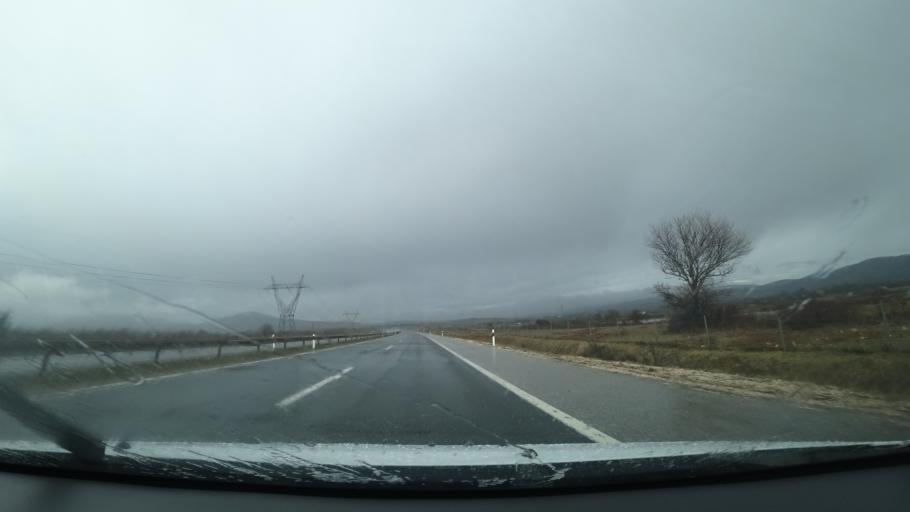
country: HR
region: Licko-Senjska
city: Gospic
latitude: 44.6050
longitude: 15.4400
